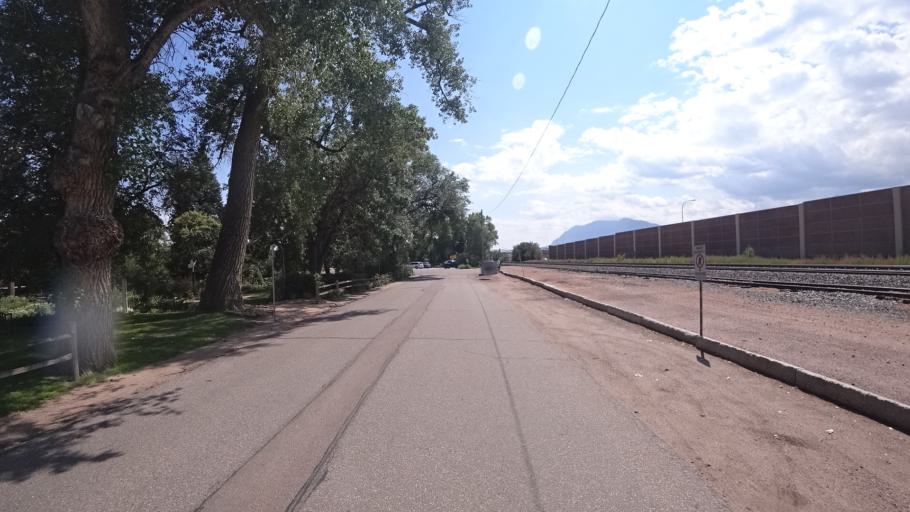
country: US
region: Colorado
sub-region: El Paso County
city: Colorado Springs
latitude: 38.8468
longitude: -104.8301
